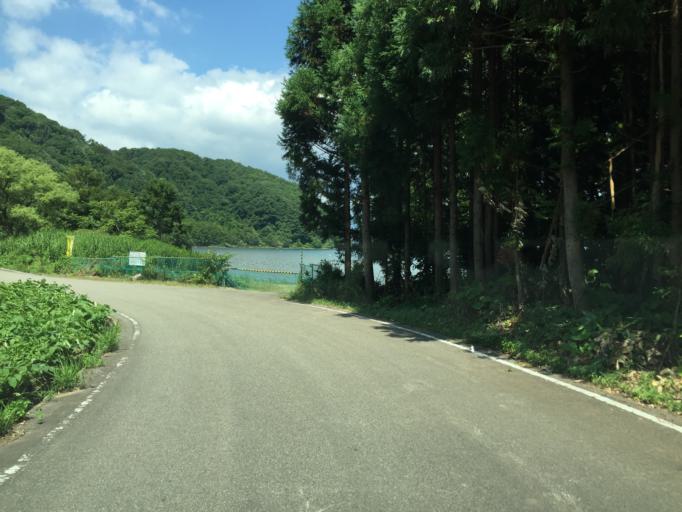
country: JP
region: Fukushima
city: Inawashiro
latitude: 37.4839
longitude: 140.0302
